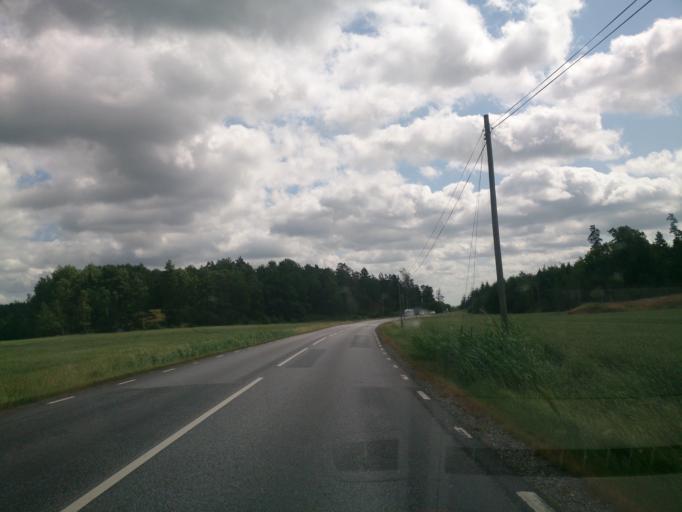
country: SE
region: OEstergoetland
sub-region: Soderkopings Kommun
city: Soederkoeping
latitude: 58.5260
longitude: 16.4441
